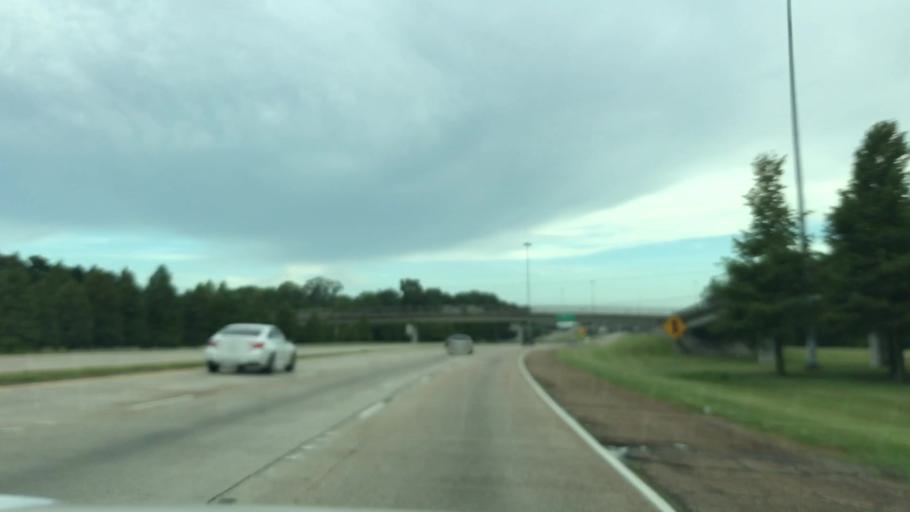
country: US
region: Louisiana
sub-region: East Baton Rouge Parish
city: Brownsfield
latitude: 30.5171
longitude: -91.1595
